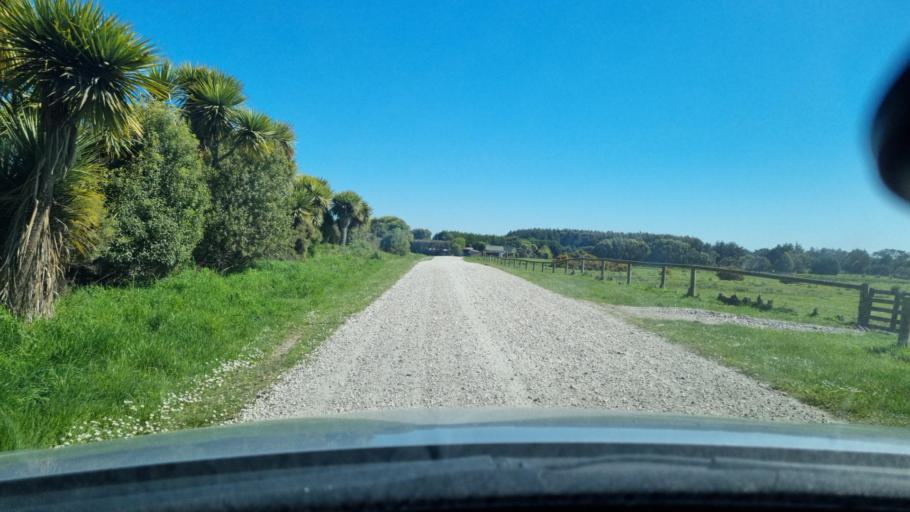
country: NZ
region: Southland
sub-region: Invercargill City
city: Invercargill
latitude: -46.4222
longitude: 168.2931
